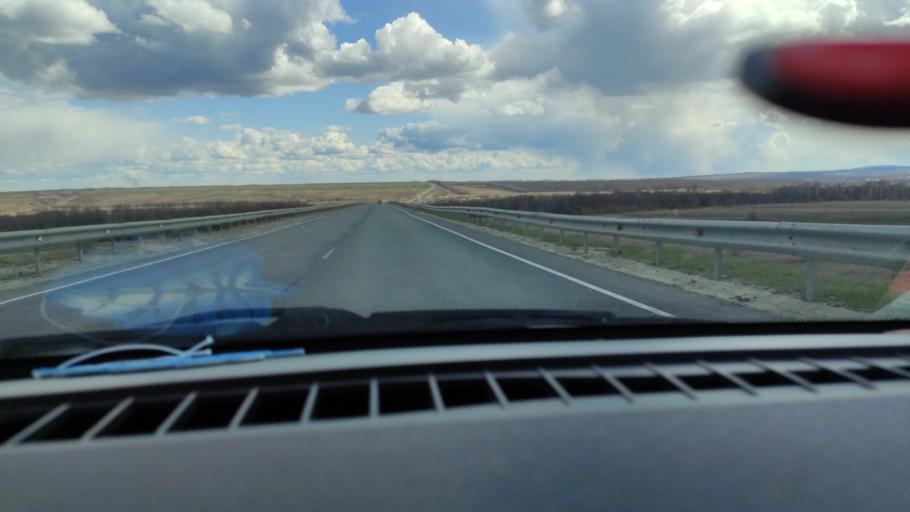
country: RU
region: Saratov
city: Dukhovnitskoye
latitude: 52.7503
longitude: 48.2487
